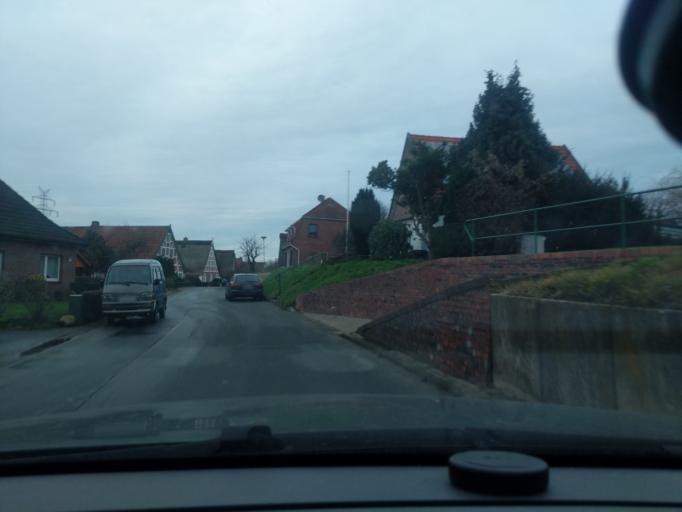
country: DE
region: Lower Saxony
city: Mittelnkirchen
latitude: 53.5353
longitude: 9.6130
